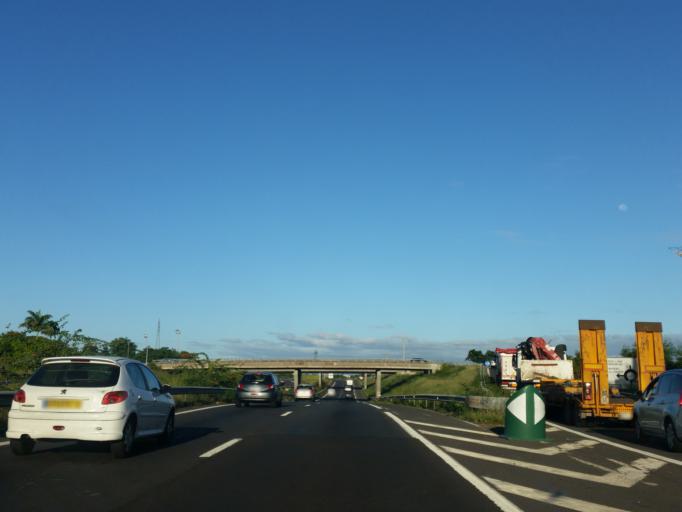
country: RE
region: Reunion
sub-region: Reunion
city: Le Port
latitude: -20.9548
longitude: 55.3130
